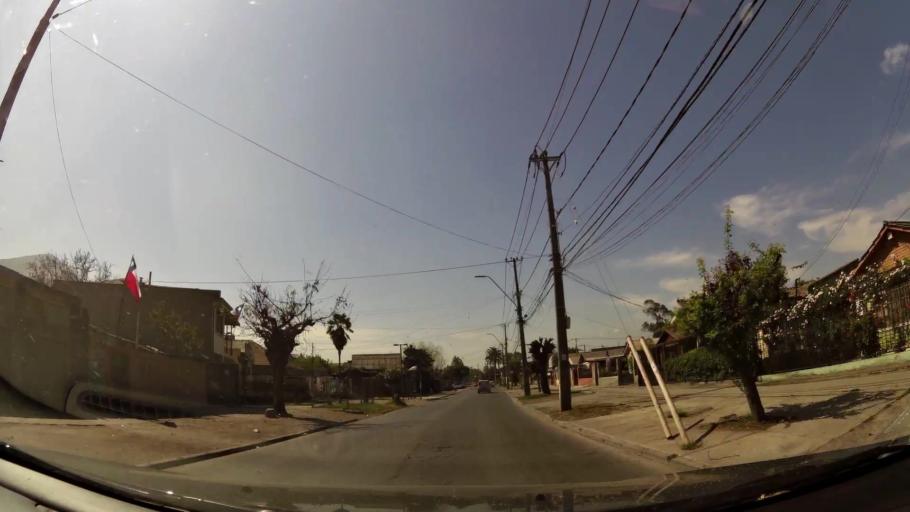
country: CL
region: Santiago Metropolitan
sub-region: Provincia de Santiago
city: Lo Prado
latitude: -33.4042
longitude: -70.7214
